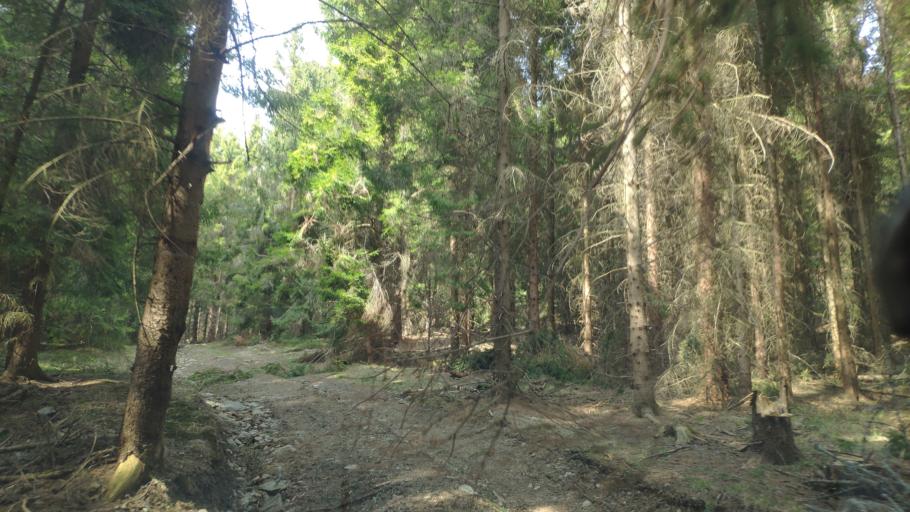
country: SK
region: Kosicky
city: Gelnica
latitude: 48.7579
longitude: 21.0197
